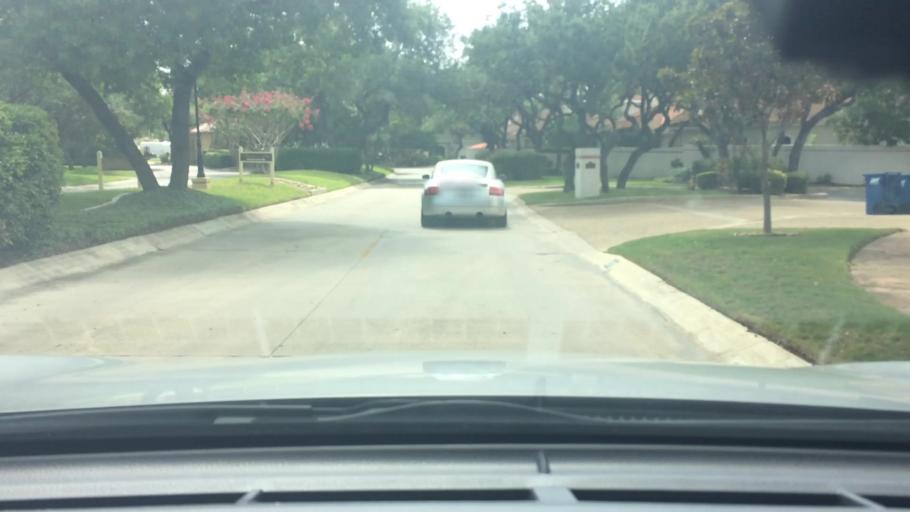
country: US
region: Texas
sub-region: Bexar County
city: Hollywood Park
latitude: 29.6162
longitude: -98.4955
